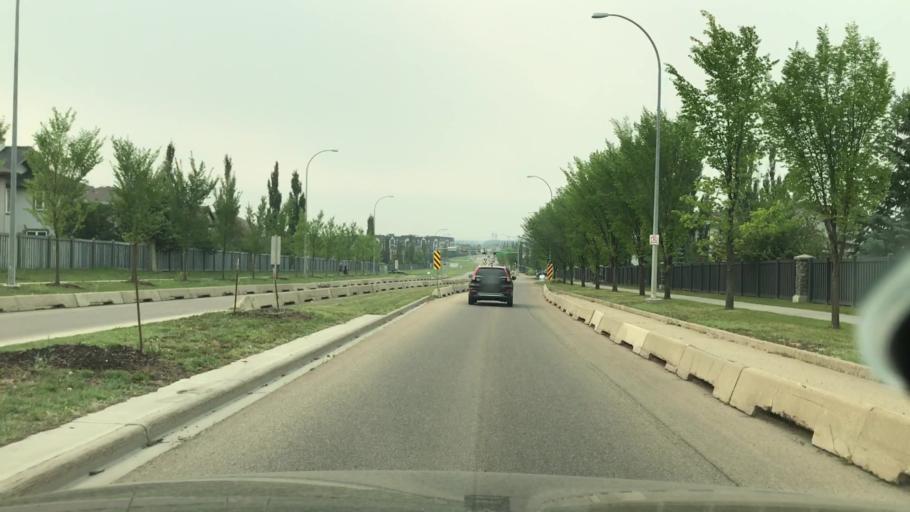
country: CA
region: Alberta
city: Edmonton
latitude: 53.4466
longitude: -113.5657
